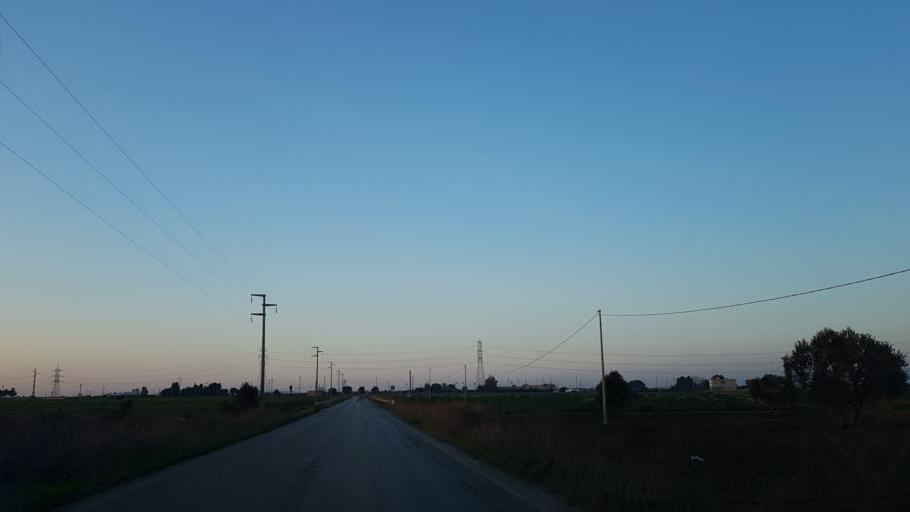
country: IT
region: Apulia
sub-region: Provincia di Brindisi
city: La Rosa
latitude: 40.5860
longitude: 17.9462
